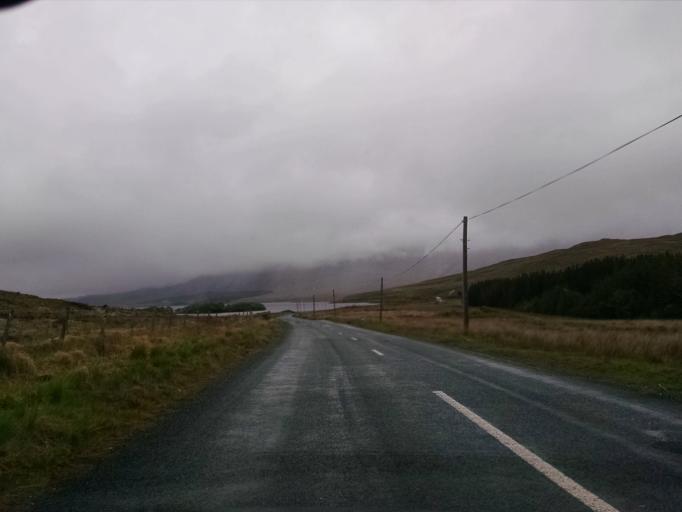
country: IE
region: Connaught
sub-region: County Galway
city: Clifden
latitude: 53.4895
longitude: -9.7389
